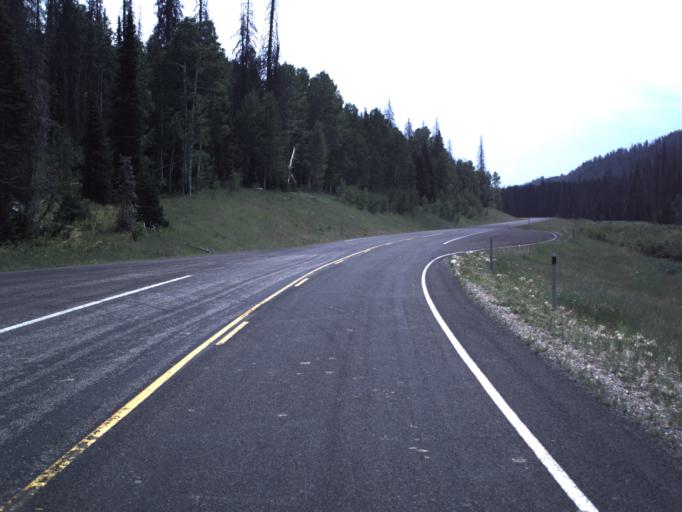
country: US
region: Utah
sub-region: Summit County
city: Francis
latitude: 40.4936
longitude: -110.9715
